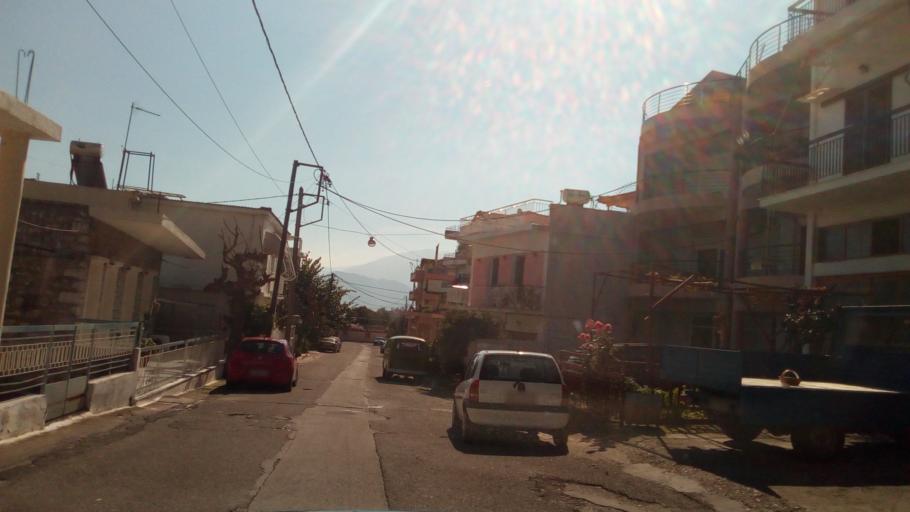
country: GR
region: West Greece
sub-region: Nomos Aitolias kai Akarnanias
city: Nafpaktos
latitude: 38.3960
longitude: 21.8445
